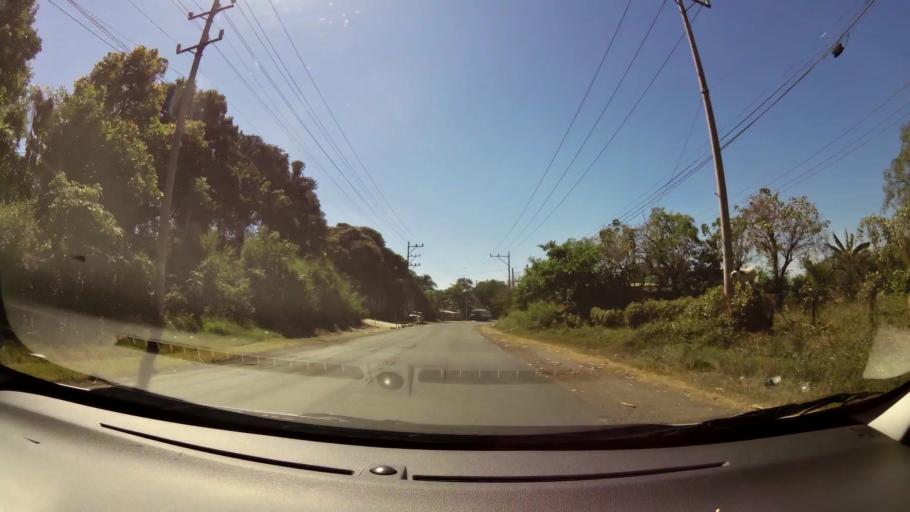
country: SV
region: La Libertad
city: San Juan Opico
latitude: 13.8040
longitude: -89.3590
